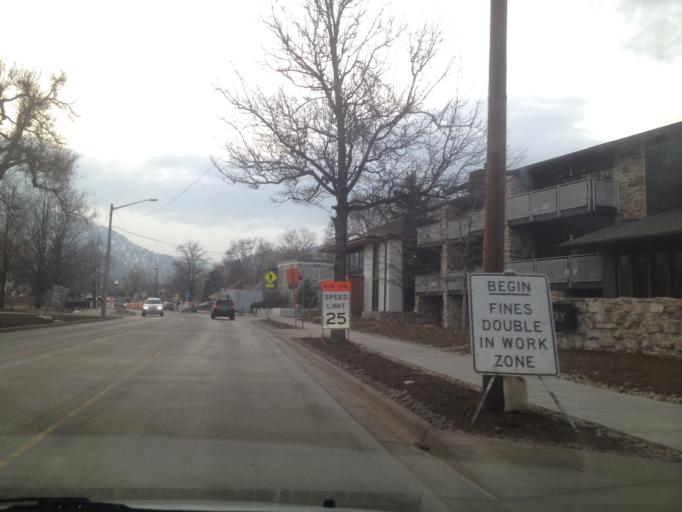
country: US
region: Colorado
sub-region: Boulder County
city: Boulder
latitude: 40.0146
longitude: -105.2753
